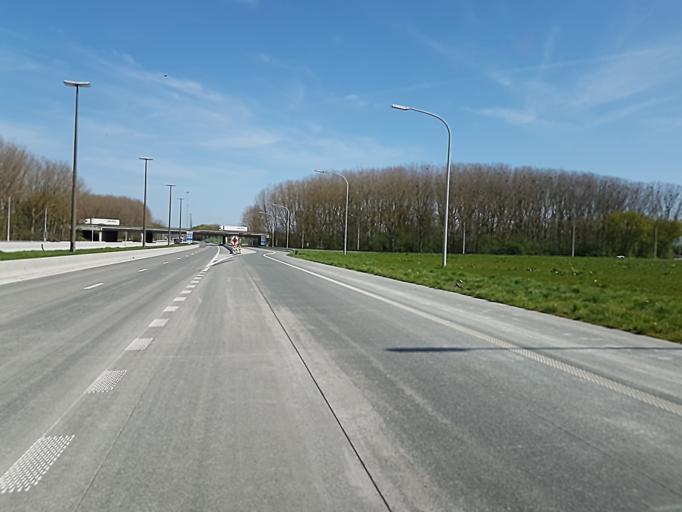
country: BE
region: Wallonia
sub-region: Province du Hainaut
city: Rumes
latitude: 50.6131
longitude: 3.3207
